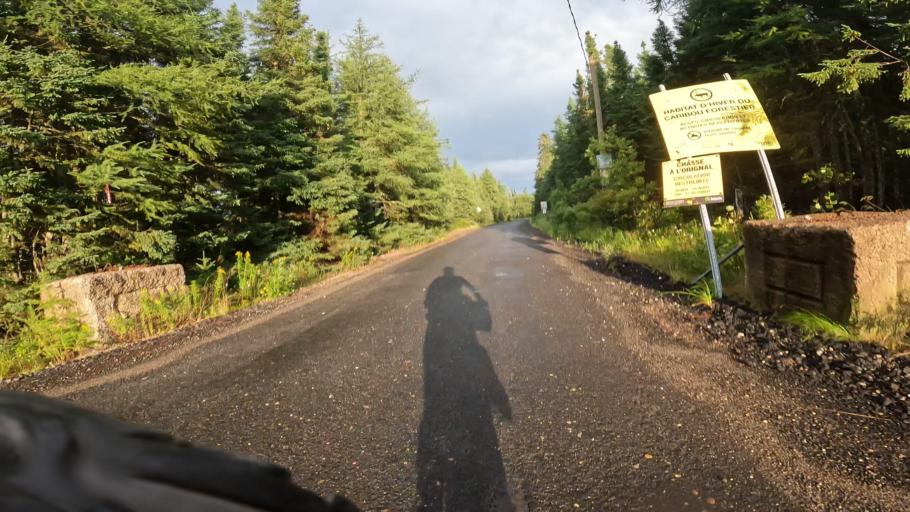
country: CA
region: Quebec
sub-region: Capitale-Nationale
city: Beaupre
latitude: 47.6386
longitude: -71.2377
